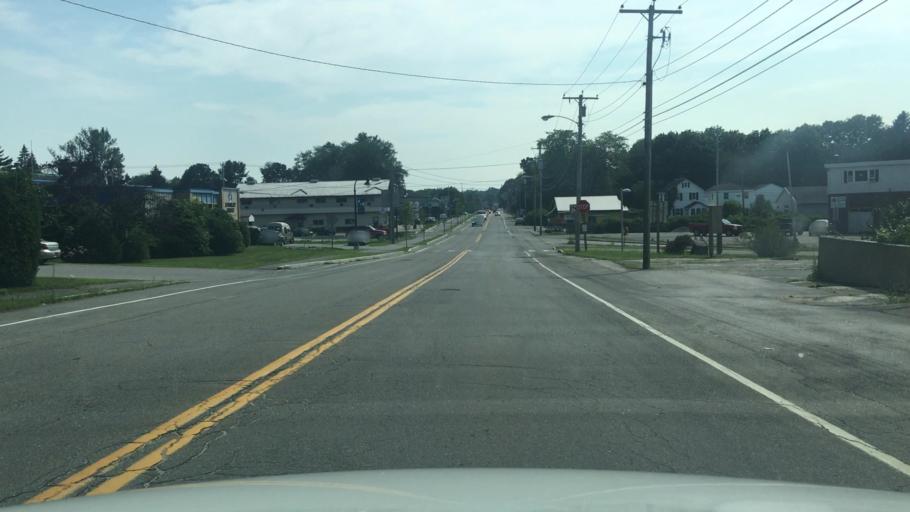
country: US
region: Maine
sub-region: Cumberland County
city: South Portland Gardens
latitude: 43.6347
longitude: -70.2878
